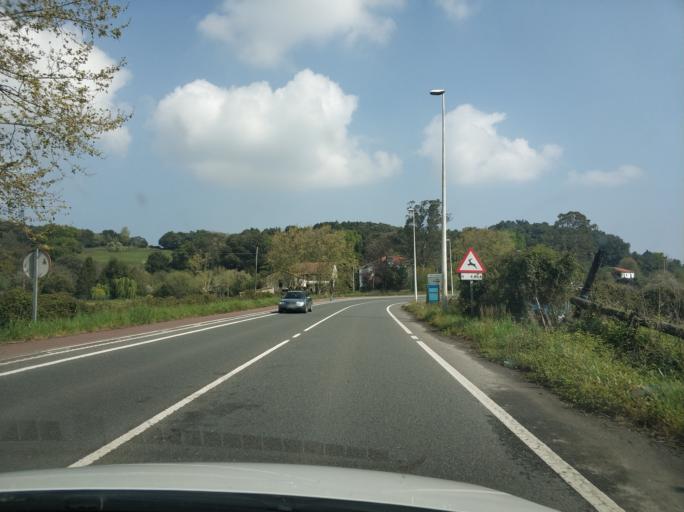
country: ES
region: Cantabria
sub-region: Provincia de Cantabria
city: Escalante
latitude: 43.4278
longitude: -3.5218
